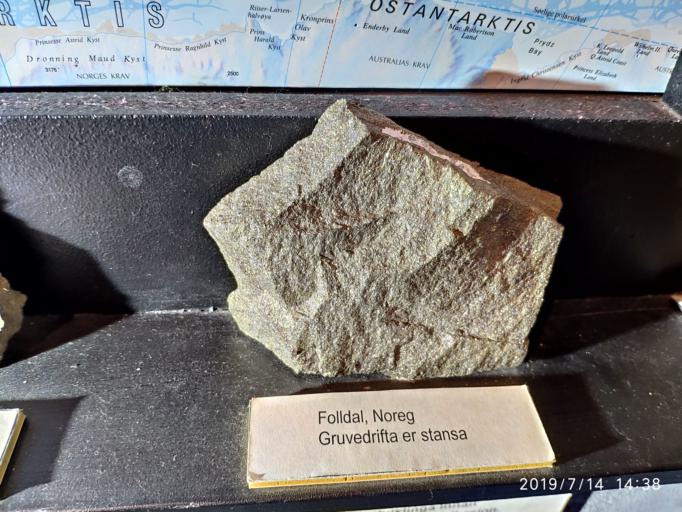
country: NO
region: Hordaland
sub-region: Odda
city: Odda
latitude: 60.1192
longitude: 6.5565
